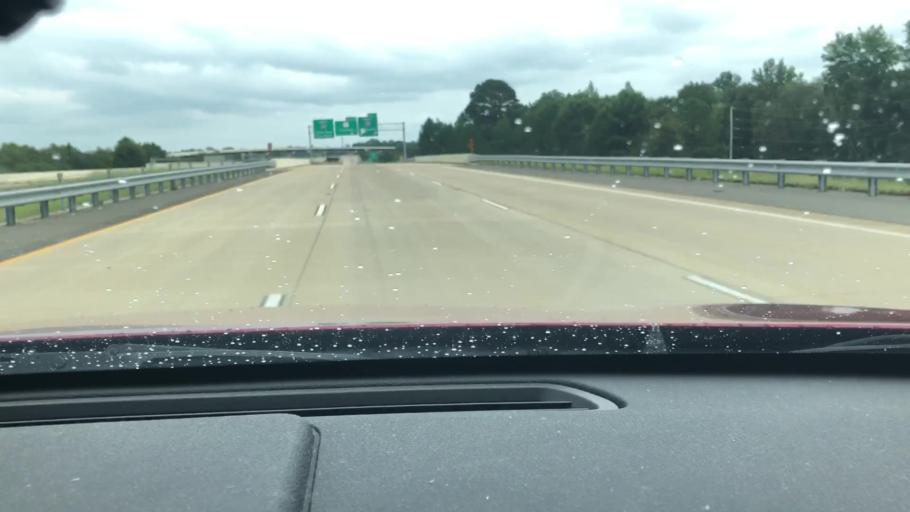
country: US
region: Texas
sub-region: Bowie County
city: Texarkana
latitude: 33.3855
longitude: -94.0275
